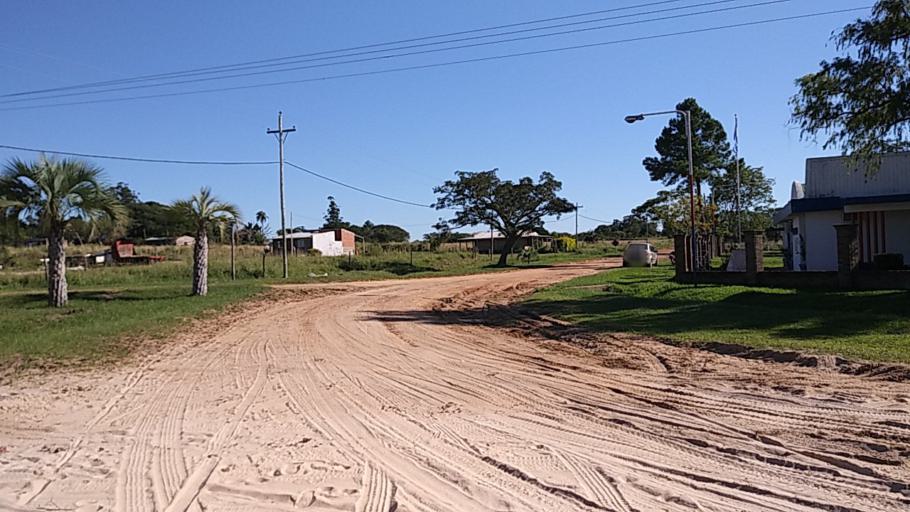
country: AR
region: Corrientes
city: Yataity Calle
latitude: -29.0300
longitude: -58.9030
